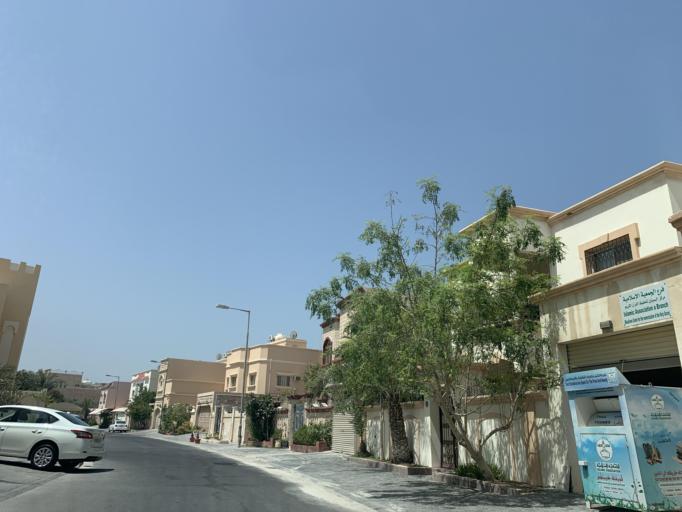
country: BH
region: Muharraq
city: Al Muharraq
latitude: 26.2779
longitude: 50.6060
